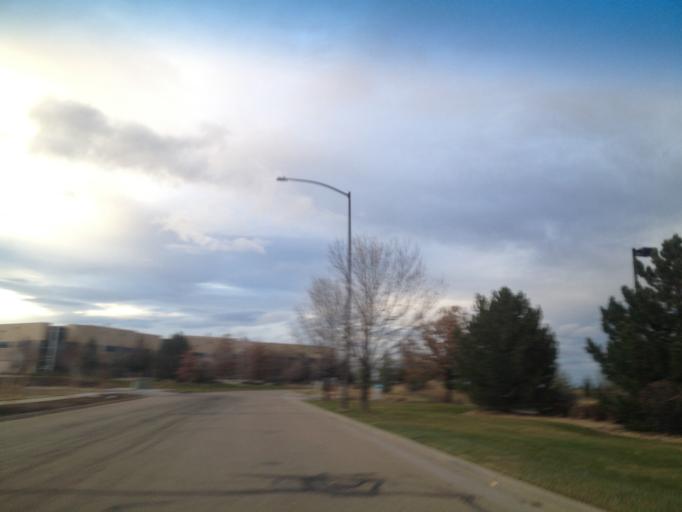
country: US
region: Colorado
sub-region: Boulder County
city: Louisville
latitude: 39.9691
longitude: -105.1196
